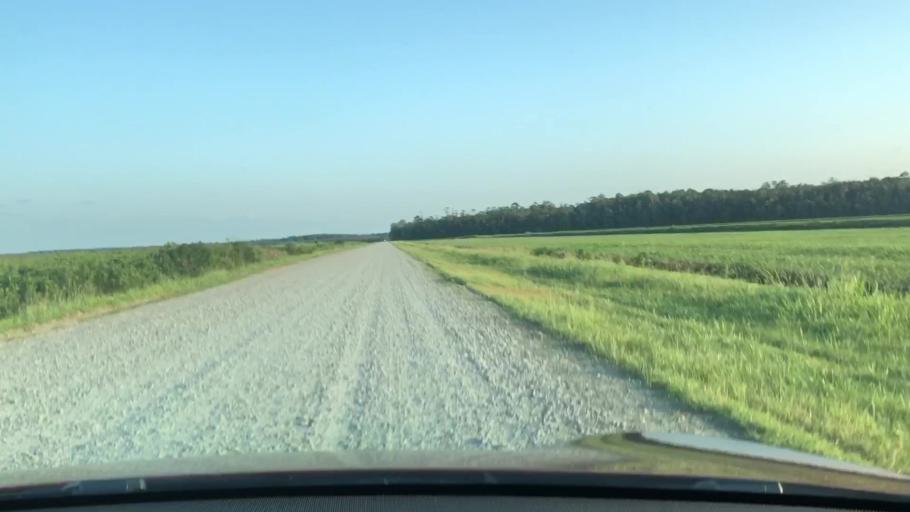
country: US
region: North Carolina
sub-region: Dare County
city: Manteo
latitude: 35.8502
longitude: -75.8615
